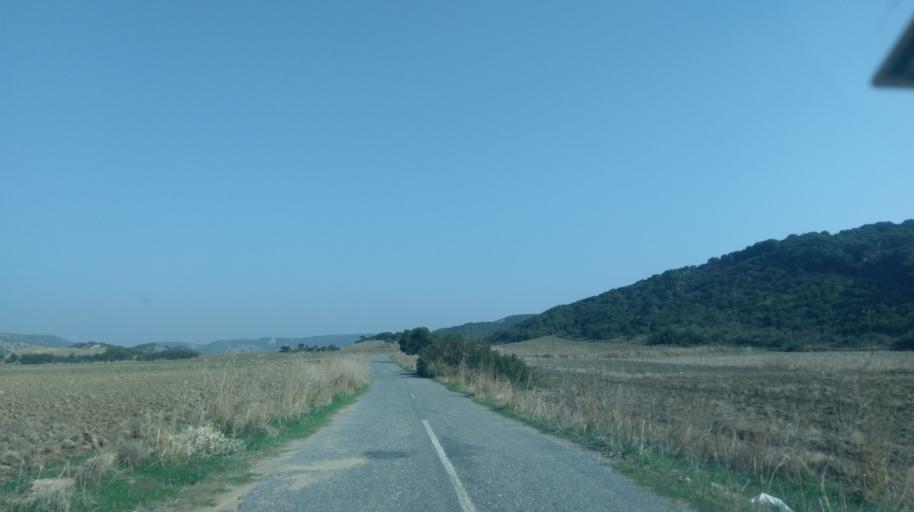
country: CY
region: Ammochostos
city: Rizokarpaso
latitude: 35.6382
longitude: 34.5127
